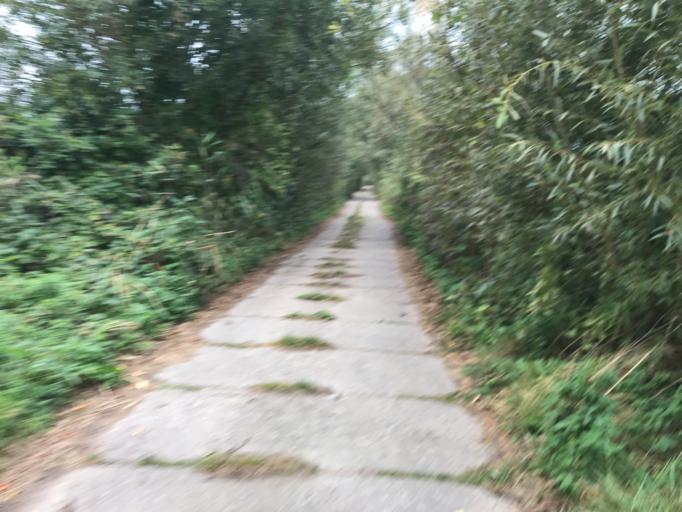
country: PL
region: Podlasie
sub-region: Powiat bialostocki
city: Tykocin
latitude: 53.1395
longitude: 22.8708
